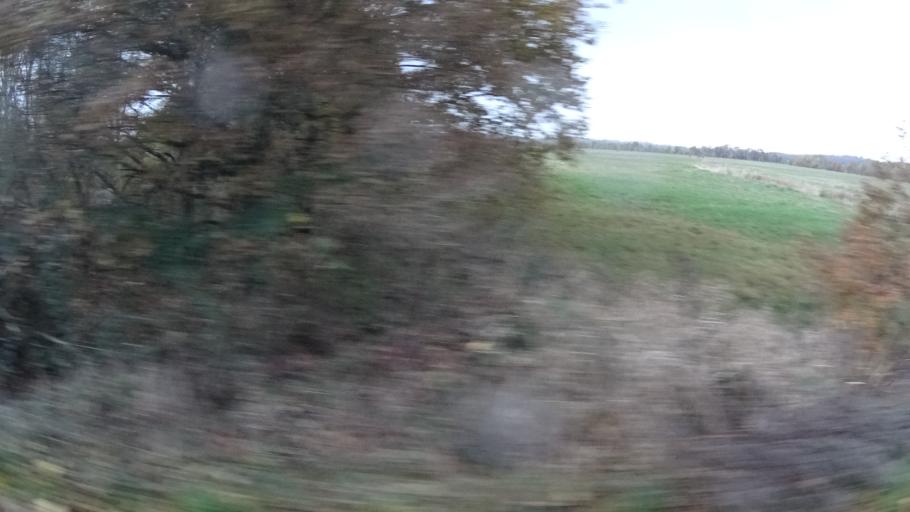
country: FR
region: Brittany
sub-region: Departement d'Ille-et-Vilaine
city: Sainte-Marie
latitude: 47.6658
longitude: -2.0286
